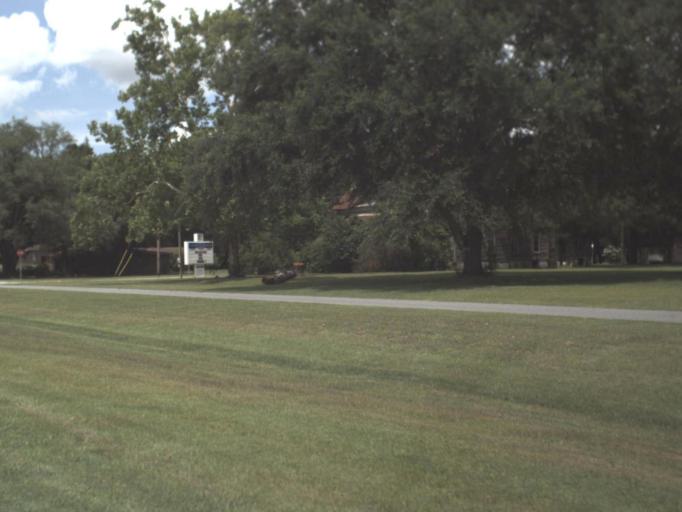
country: US
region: Florida
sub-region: Madison County
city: Madison
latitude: 30.5496
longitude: -83.3675
